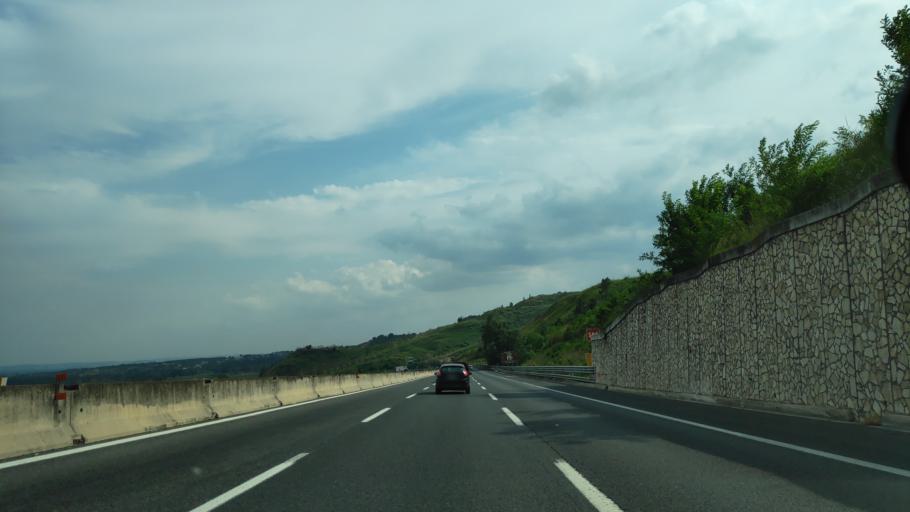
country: IT
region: Latium
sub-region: Citta metropolitana di Roma Capitale
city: Nazzano
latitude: 42.2045
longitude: 12.6031
